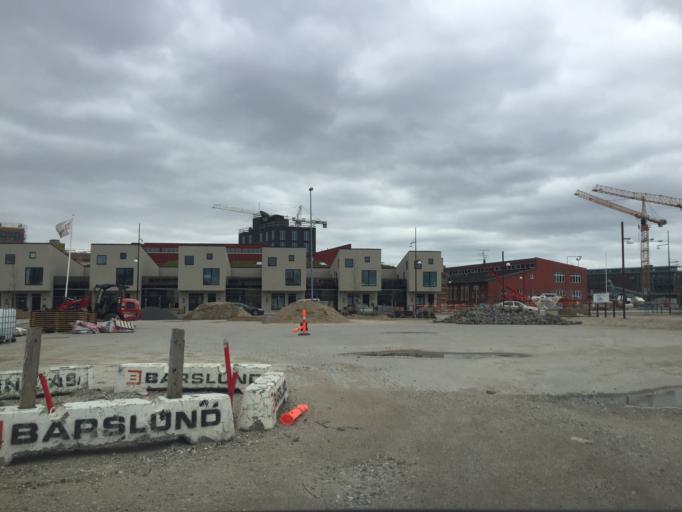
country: DK
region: Capital Region
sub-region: Kobenhavn
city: Christianshavn
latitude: 55.7091
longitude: 12.5948
